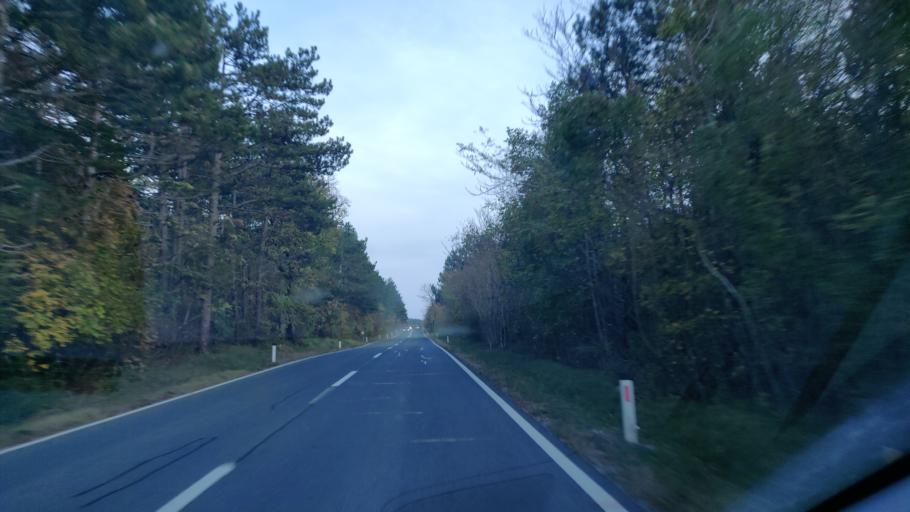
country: SI
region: Divaca
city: Divaca
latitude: 45.7372
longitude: 13.9465
